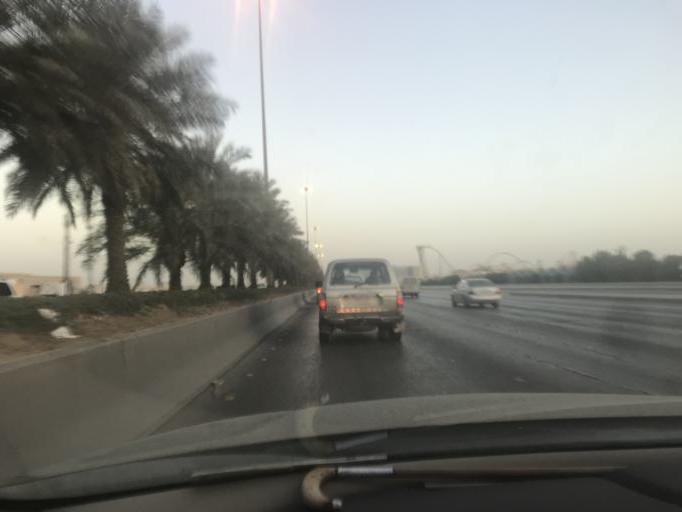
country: SA
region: Ar Riyad
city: Riyadh
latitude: 24.7689
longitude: 46.7344
